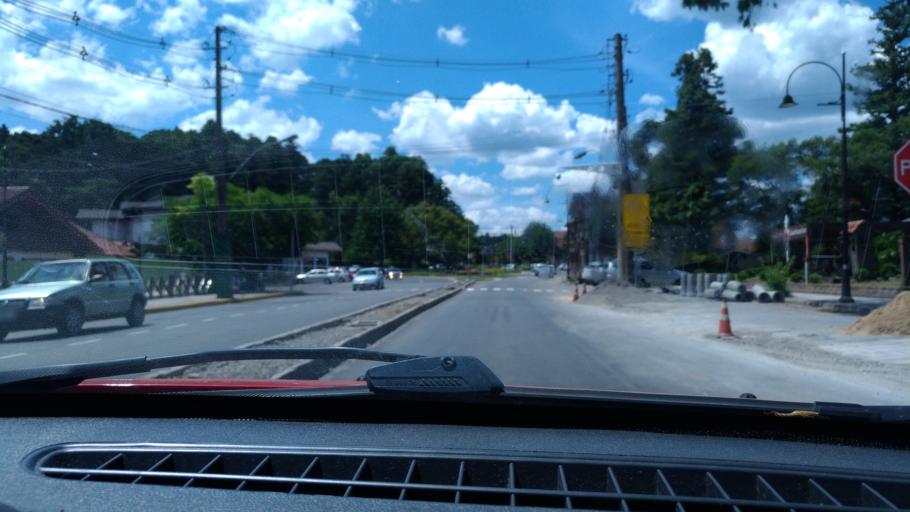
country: BR
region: Rio Grande do Sul
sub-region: Canela
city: Canela
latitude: -29.3866
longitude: -50.8739
